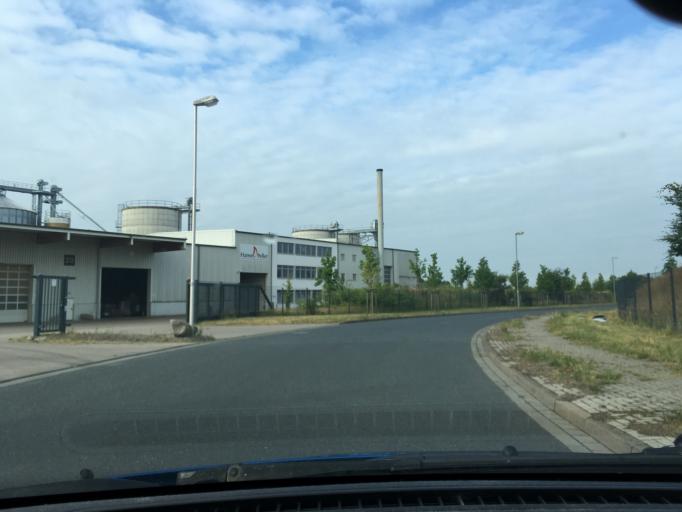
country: DE
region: Lower Saxony
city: Buchholz in der Nordheide
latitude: 53.3255
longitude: 9.8222
